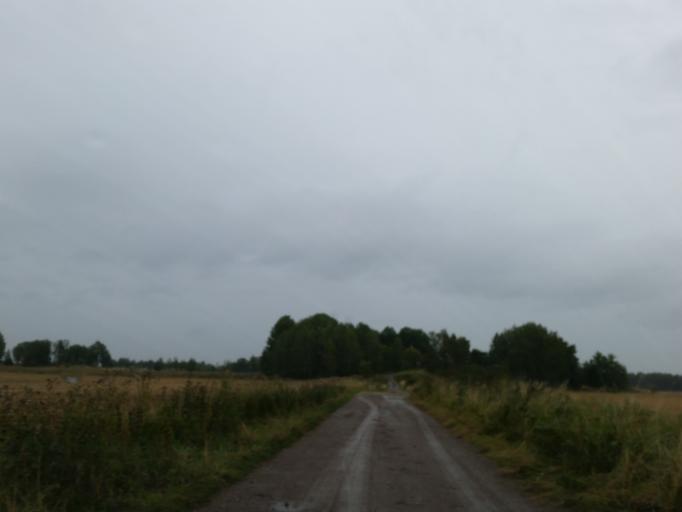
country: SE
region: Uppsala
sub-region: Habo Kommun
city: Balsta
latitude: 59.6469
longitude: 17.4800
